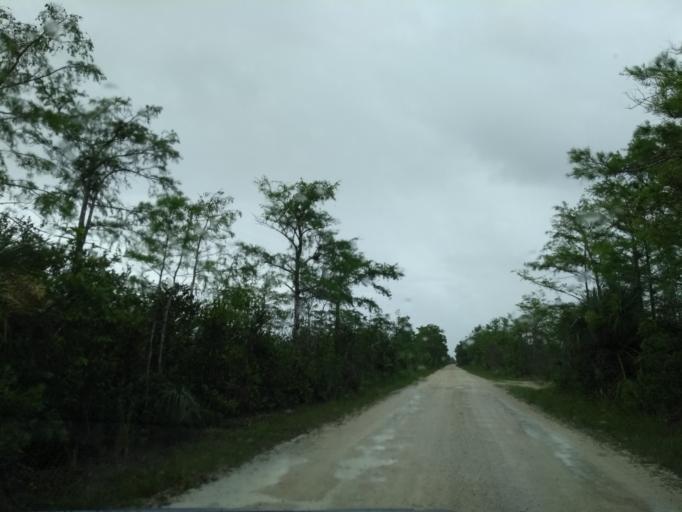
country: US
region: Florida
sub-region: Miami-Dade County
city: The Hammocks
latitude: 25.7603
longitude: -81.0145
